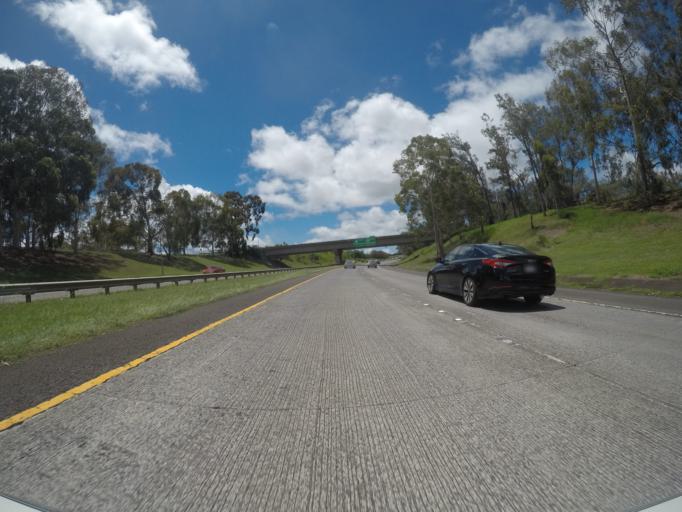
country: US
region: Hawaii
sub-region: Honolulu County
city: Waipi'o Acres
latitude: 21.4793
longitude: -158.0240
